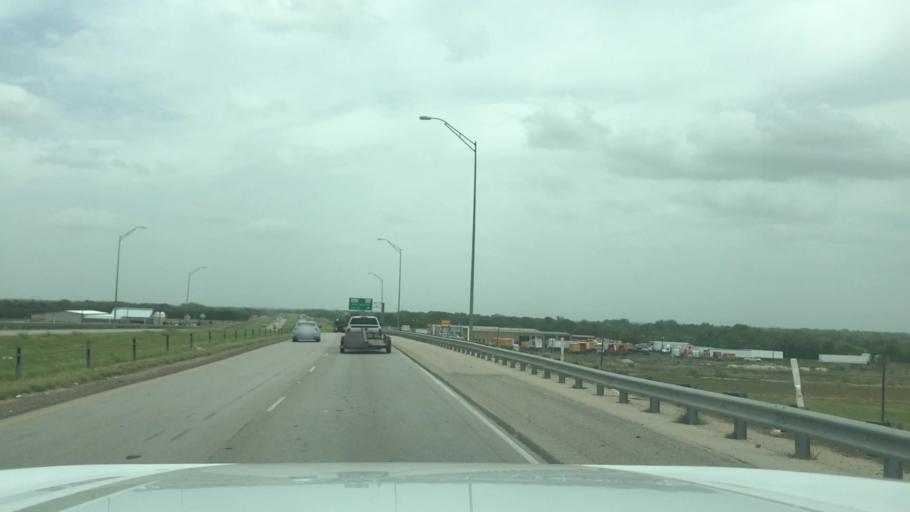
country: US
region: Texas
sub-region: McLennan County
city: Beverly
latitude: 31.5092
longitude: -97.1029
